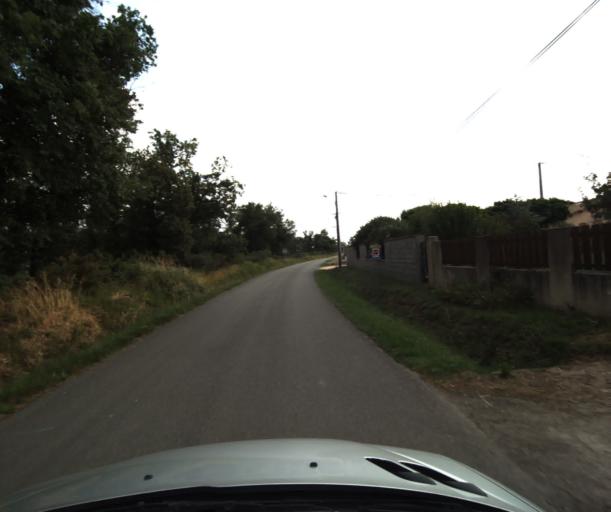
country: FR
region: Midi-Pyrenees
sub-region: Departement de la Haute-Garonne
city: Saint-Lys
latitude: 43.4974
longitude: 1.2024
